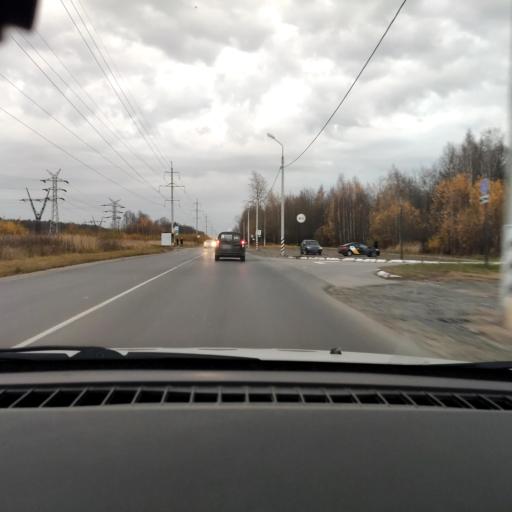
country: RU
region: Perm
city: Perm
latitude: 58.0968
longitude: 56.3974
